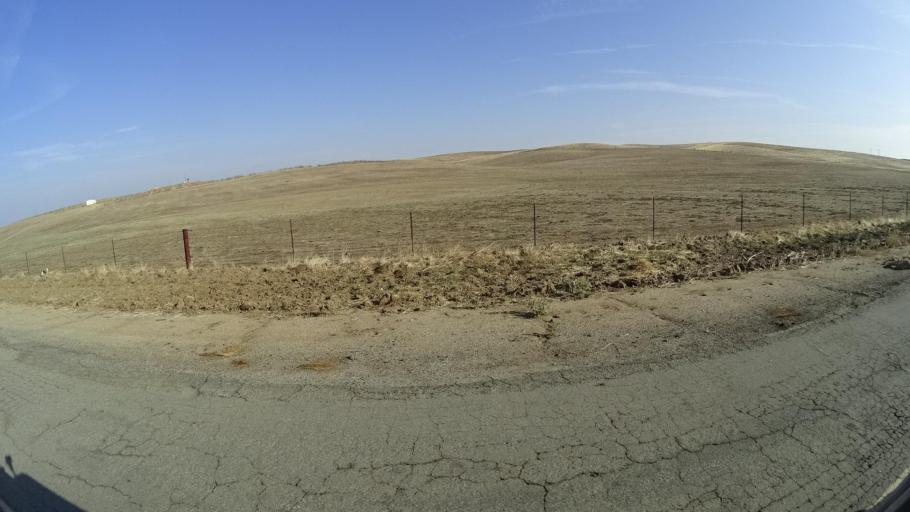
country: US
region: California
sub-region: Tulare County
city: Richgrove
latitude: 35.6473
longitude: -119.0577
